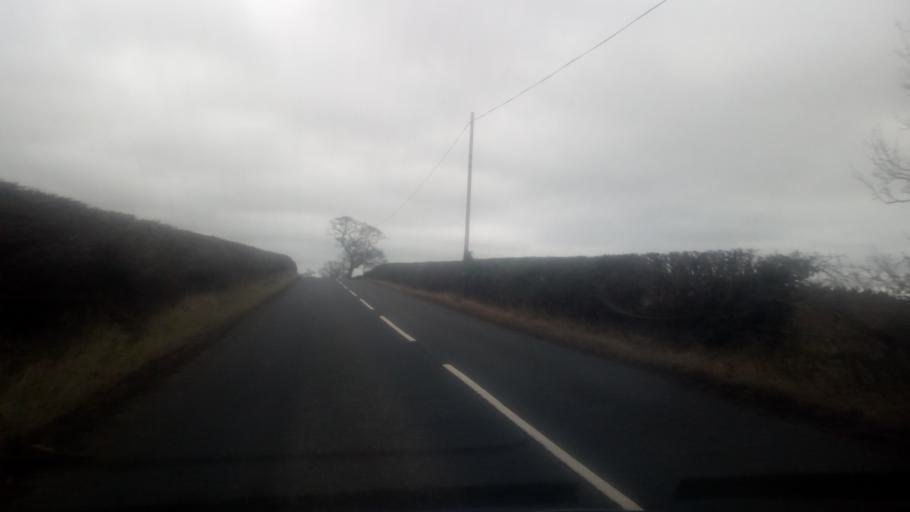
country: GB
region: Scotland
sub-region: The Scottish Borders
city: Kelso
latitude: 55.5799
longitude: -2.5034
